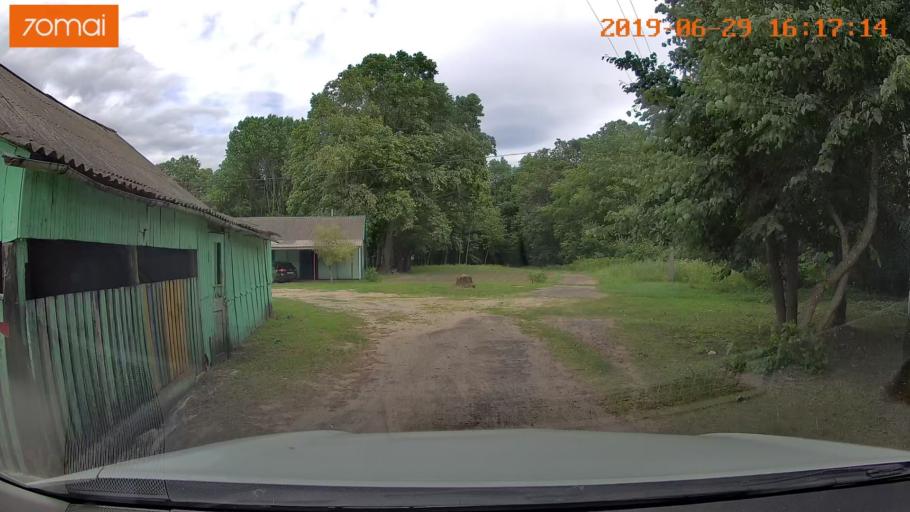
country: BY
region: Brest
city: Luninyets
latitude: 52.1998
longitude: 27.0110
